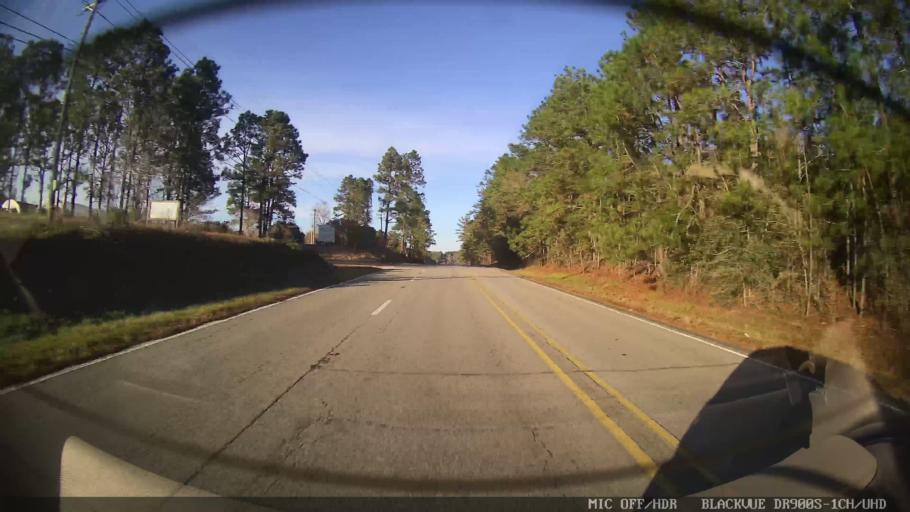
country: US
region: Mississippi
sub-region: Lamar County
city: Purvis
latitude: 31.1045
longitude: -89.4124
